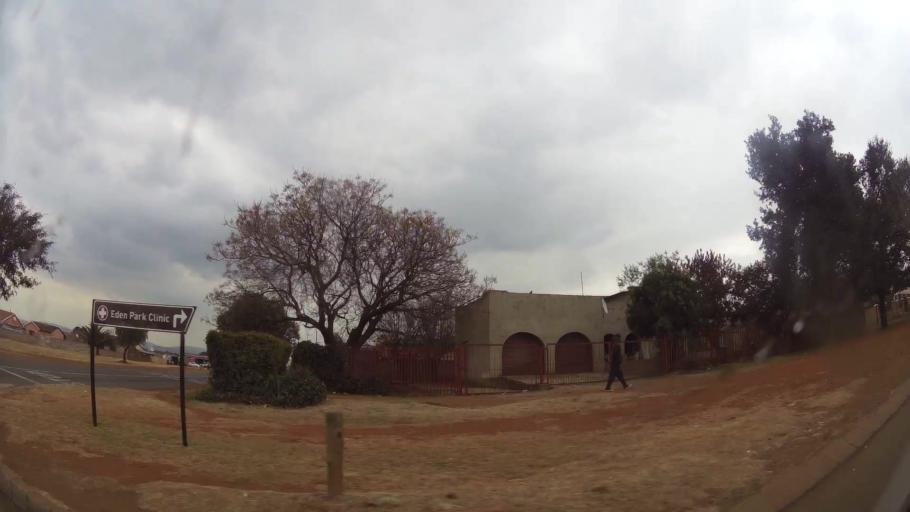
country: ZA
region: Gauteng
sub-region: Ekurhuleni Metropolitan Municipality
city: Germiston
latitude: -26.3820
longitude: 28.1265
